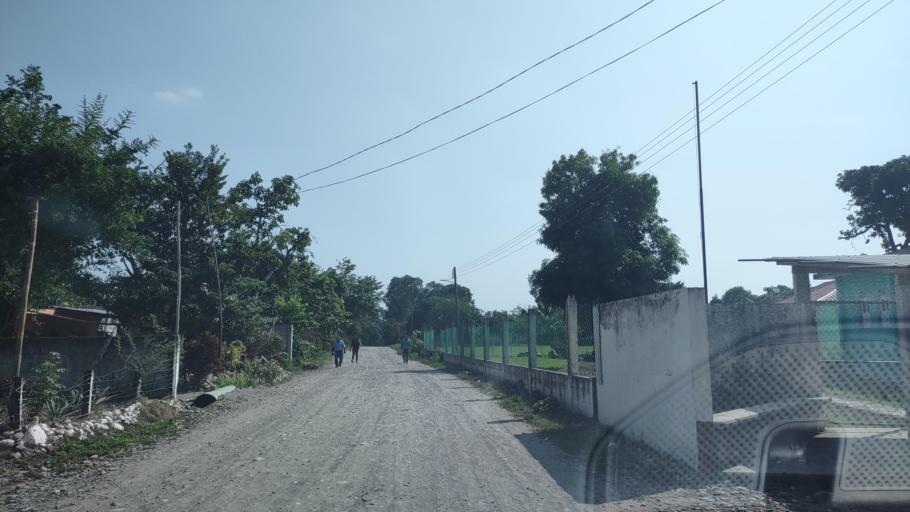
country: MX
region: Veracruz
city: Agua Dulce
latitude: 20.2738
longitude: -97.2849
